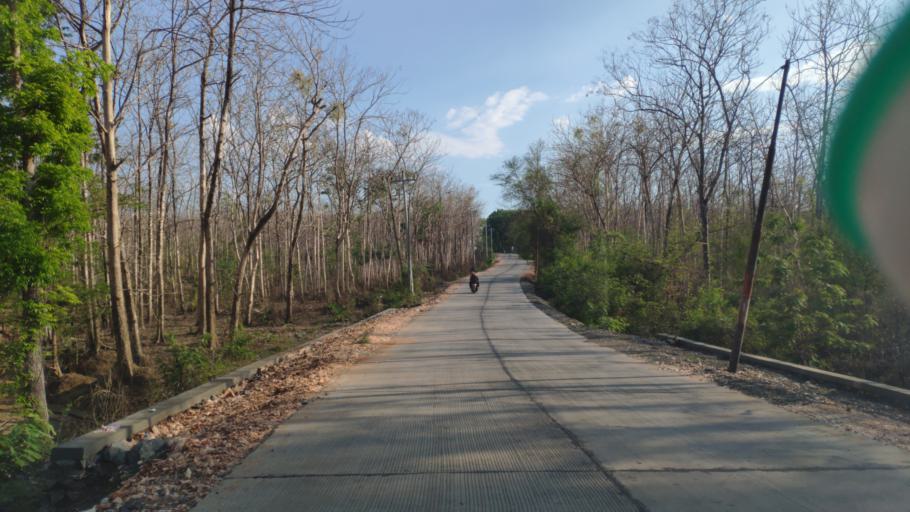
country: ID
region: Central Java
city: Ploso Wetan
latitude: -7.1594
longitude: 111.4115
